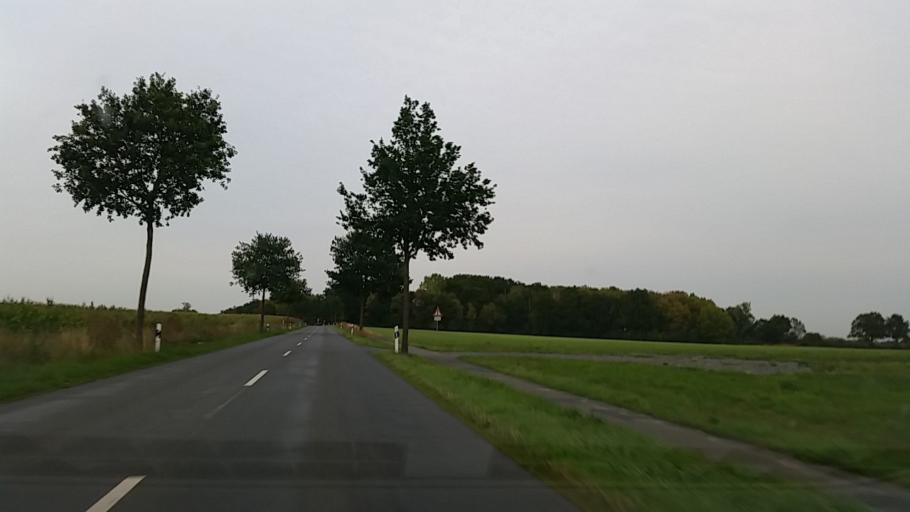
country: DE
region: Lower Saxony
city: Klein Schwulper
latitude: 52.3416
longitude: 10.4529
